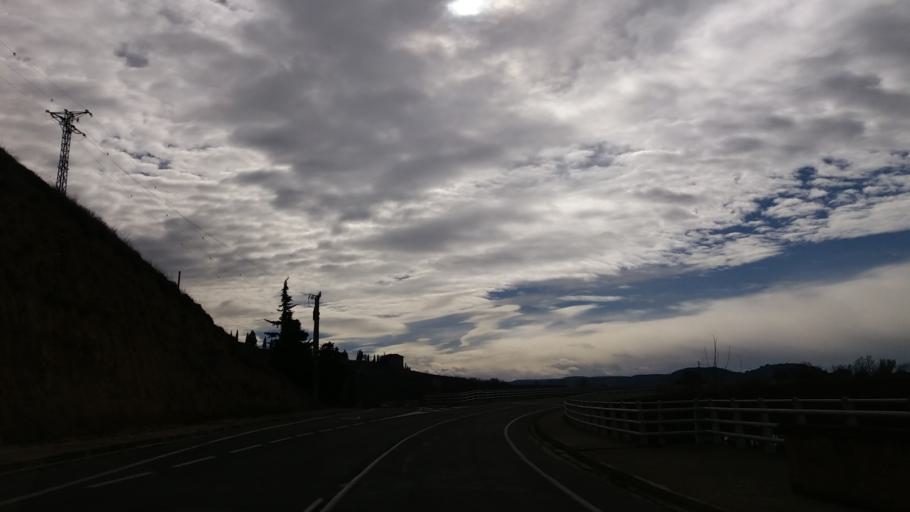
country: ES
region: La Rioja
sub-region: Provincia de La Rioja
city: San Vicente de la Sonsierra
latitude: 42.5596
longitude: -2.7596
